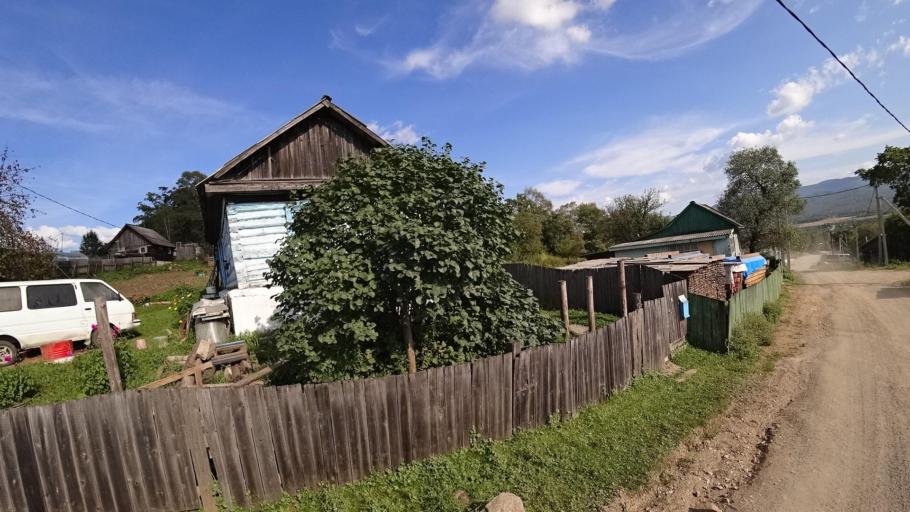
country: RU
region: Jewish Autonomous Oblast
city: Birakan
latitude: 48.9979
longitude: 131.7122
